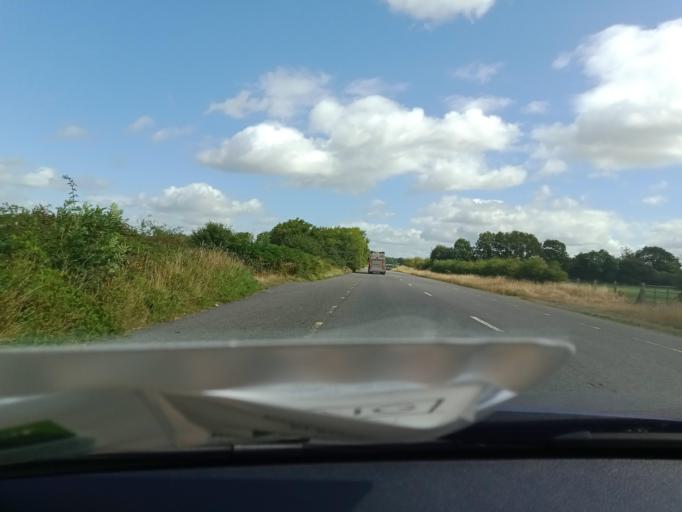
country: IE
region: Leinster
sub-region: Laois
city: Abbeyleix
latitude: 52.8325
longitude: -7.4449
